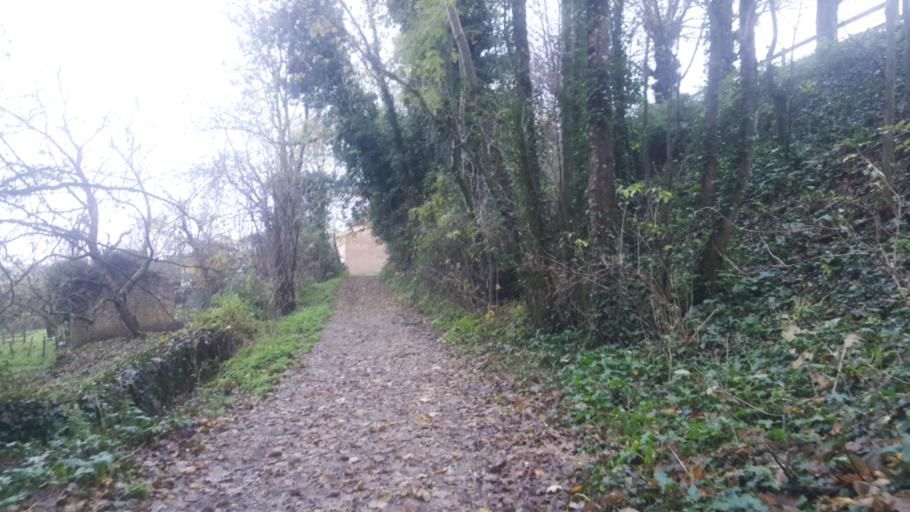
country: FR
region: Poitou-Charentes
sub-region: Departement des Deux-Sevres
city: Melle
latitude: 46.2259
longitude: -0.1496
